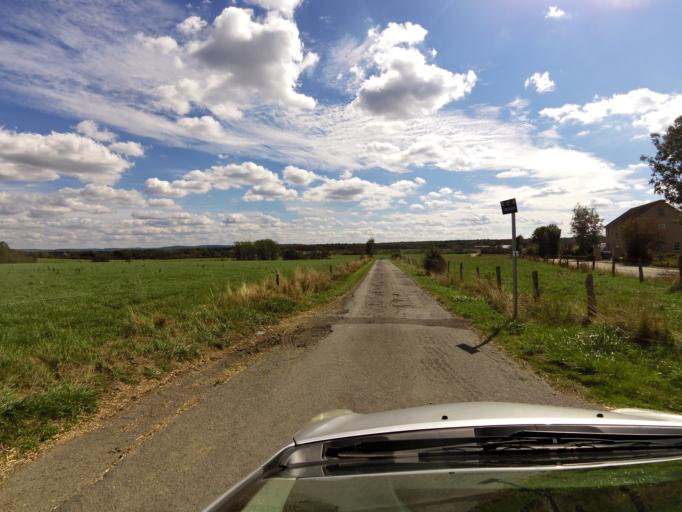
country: BE
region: Wallonia
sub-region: Province du Luxembourg
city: Durbuy
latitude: 50.3281
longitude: 5.4160
